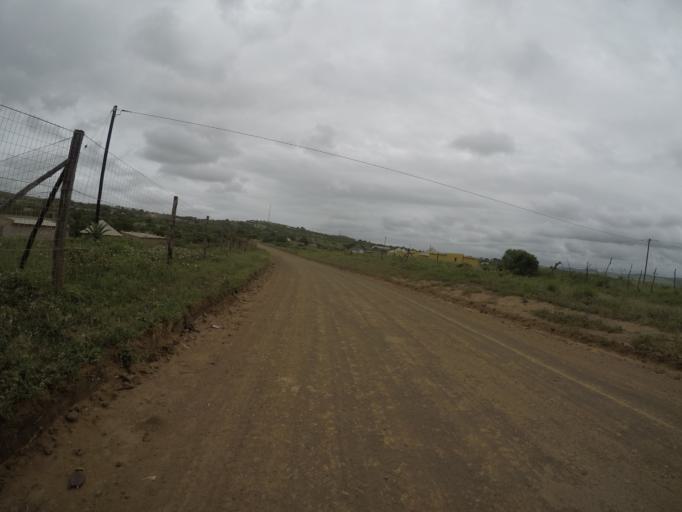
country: ZA
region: KwaZulu-Natal
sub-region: uThungulu District Municipality
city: Empangeni
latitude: -28.5966
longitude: 31.8385
